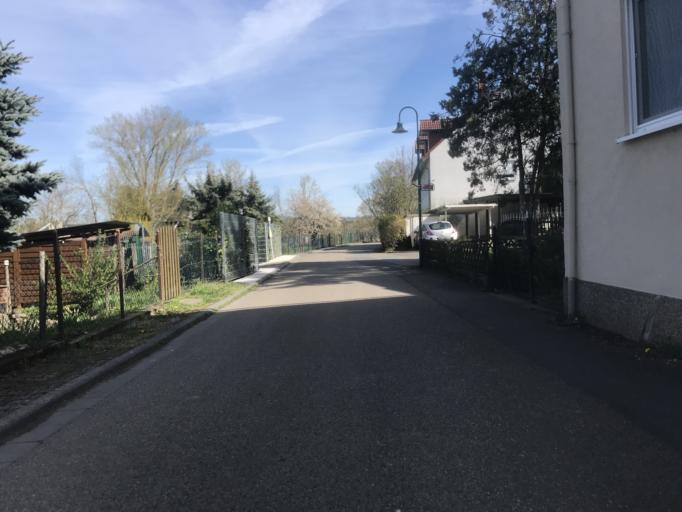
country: DE
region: Rheinland-Pfalz
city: Stadecken-Elsheim
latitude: 49.9141
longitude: 8.1372
